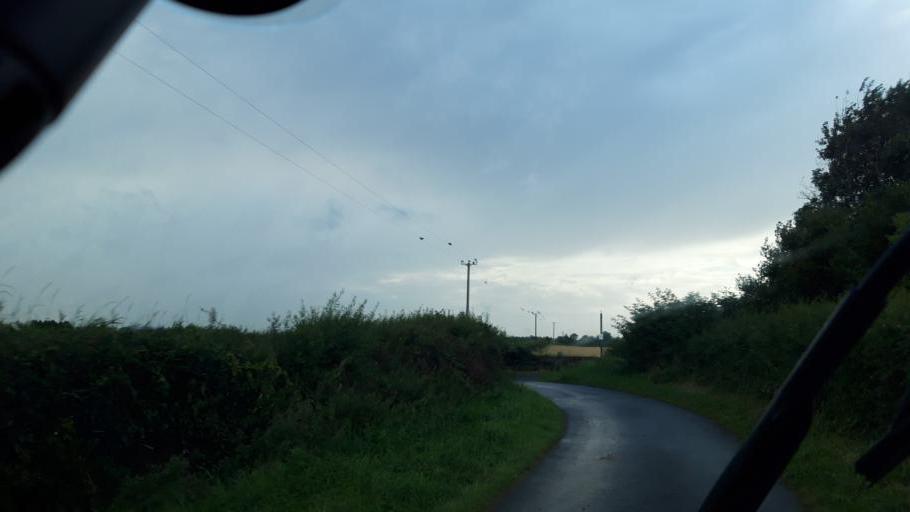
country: IE
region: Leinster
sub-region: Kildare
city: Leixlip
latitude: 53.3427
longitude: -6.4901
